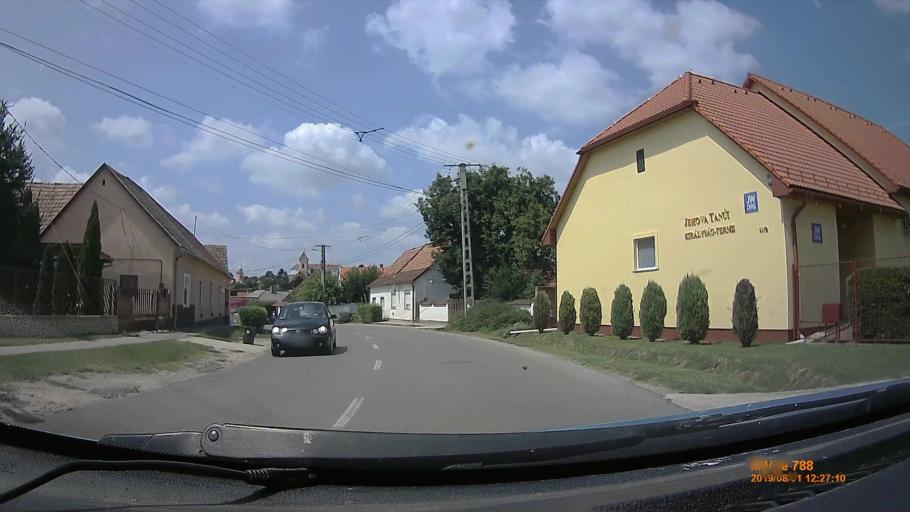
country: HU
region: Baranya
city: Siklos
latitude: 45.8523
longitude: 18.3050
